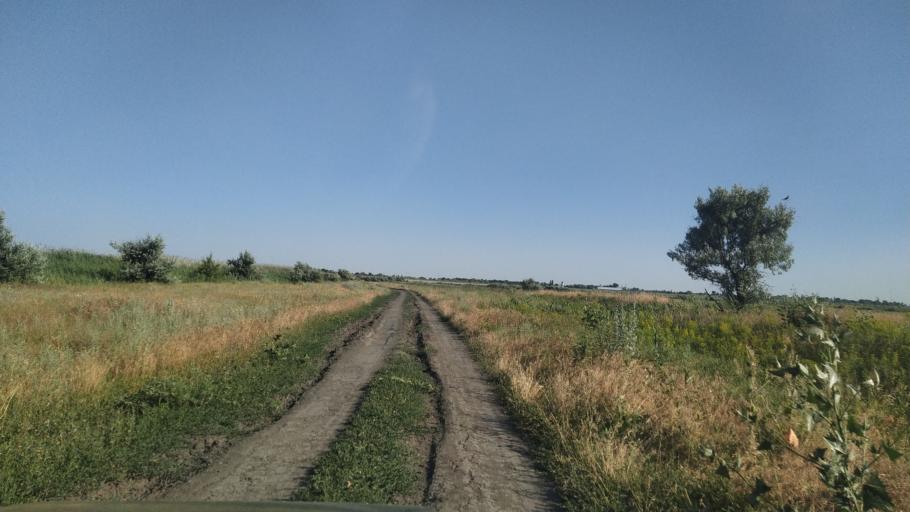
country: RU
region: Rostov
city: Kuleshovka
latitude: 47.1246
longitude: 39.6470
